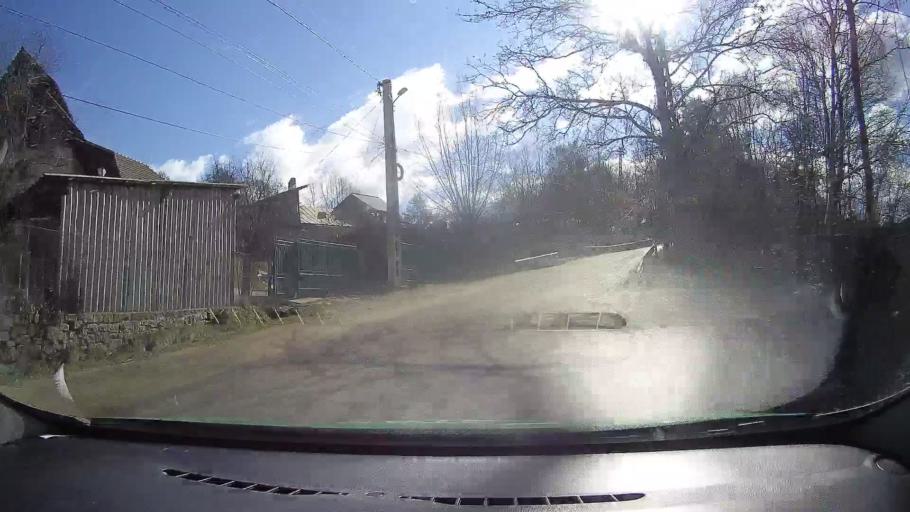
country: RO
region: Dambovita
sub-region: Comuna Runcu
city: Badeni
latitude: 45.1485
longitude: 25.4034
